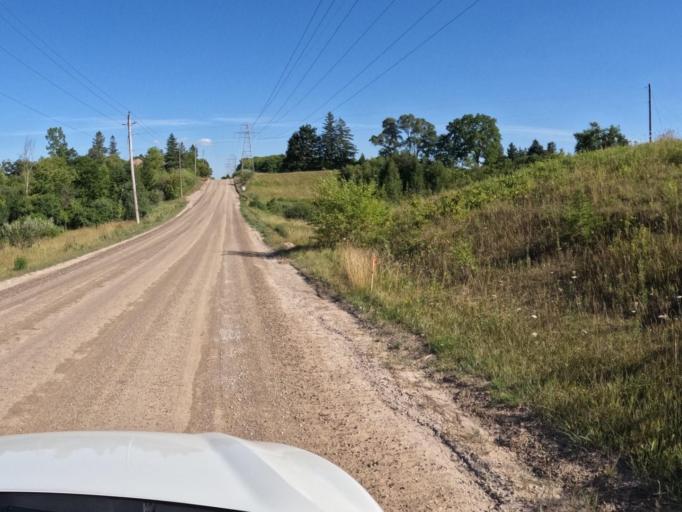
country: CA
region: Ontario
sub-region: Wellington County
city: Guelph
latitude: 43.4404
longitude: -80.1435
